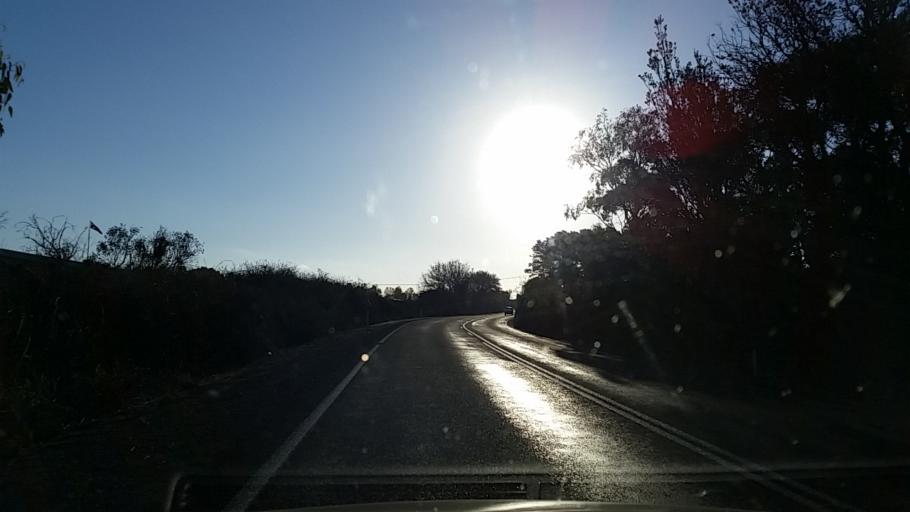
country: AU
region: South Australia
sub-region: Alexandrina
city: Mount Compass
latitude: -35.3587
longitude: 138.7230
